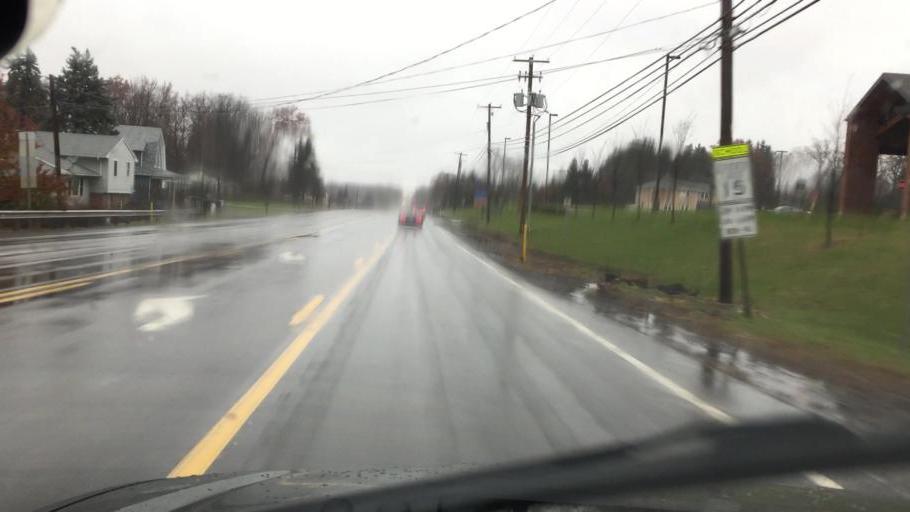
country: US
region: Pennsylvania
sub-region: Luzerne County
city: Mountain Top
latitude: 41.1208
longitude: -75.9096
